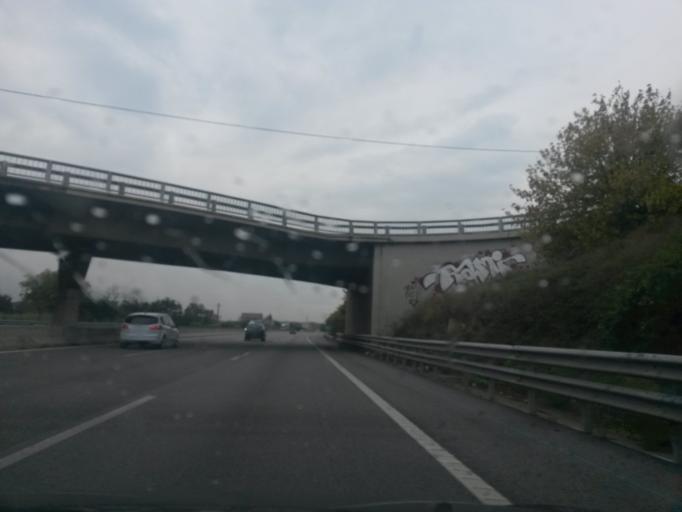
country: ES
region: Catalonia
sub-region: Provincia de Barcelona
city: Llinars del Valles
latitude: 41.6350
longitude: 2.4030
